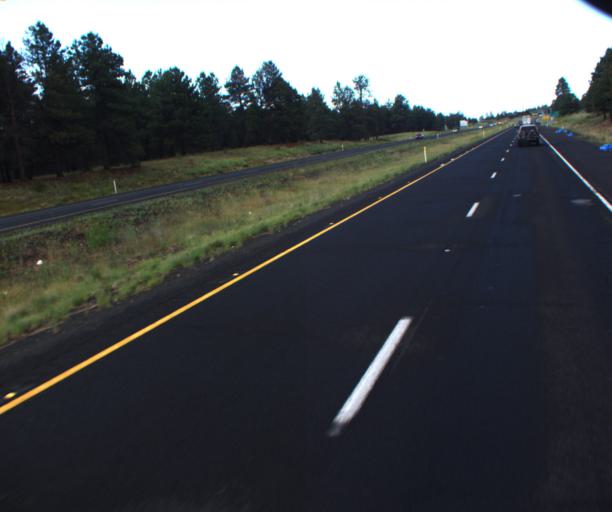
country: US
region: Arizona
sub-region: Coconino County
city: Kachina Village
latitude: 35.1504
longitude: -111.6817
